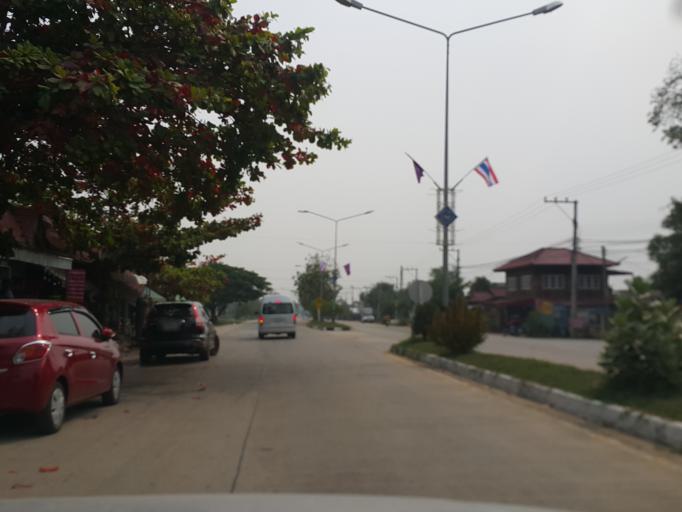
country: TH
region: Lampang
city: Ko Kha
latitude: 18.1929
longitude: 99.4020
